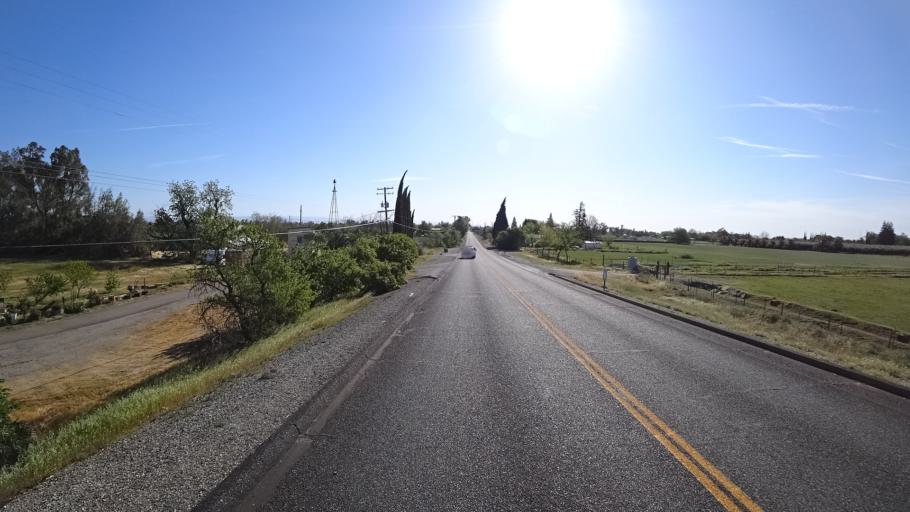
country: US
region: California
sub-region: Glenn County
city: Orland
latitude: 39.7258
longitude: -122.2046
